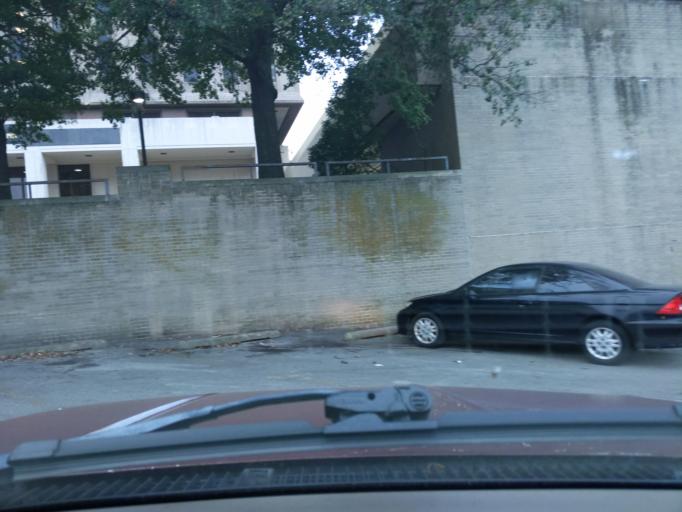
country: US
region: Oklahoma
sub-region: Tulsa County
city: Tulsa
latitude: 36.1348
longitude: -95.9678
